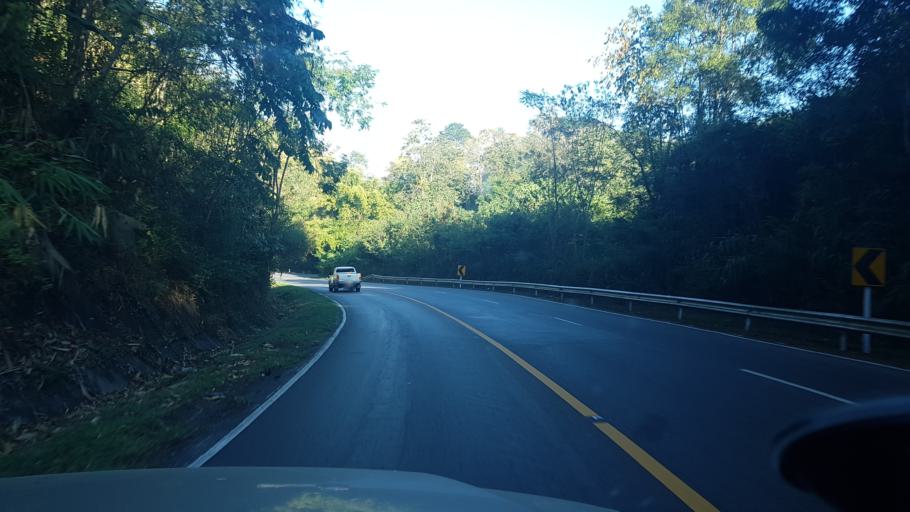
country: TH
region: Phetchabun
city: Nam Nao
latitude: 16.7535
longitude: 101.4965
